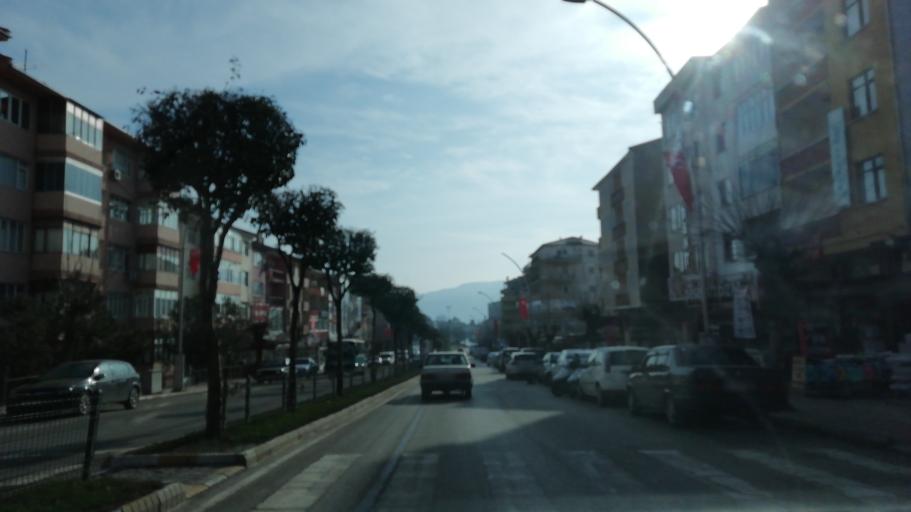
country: TR
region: Karabuk
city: Safranbolu
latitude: 41.2526
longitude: 32.6793
